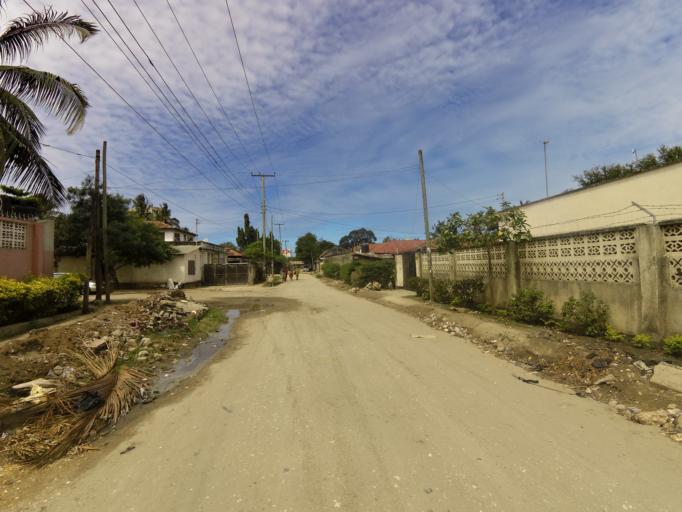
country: TZ
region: Dar es Salaam
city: Magomeni
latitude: -6.8077
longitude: 39.2529
